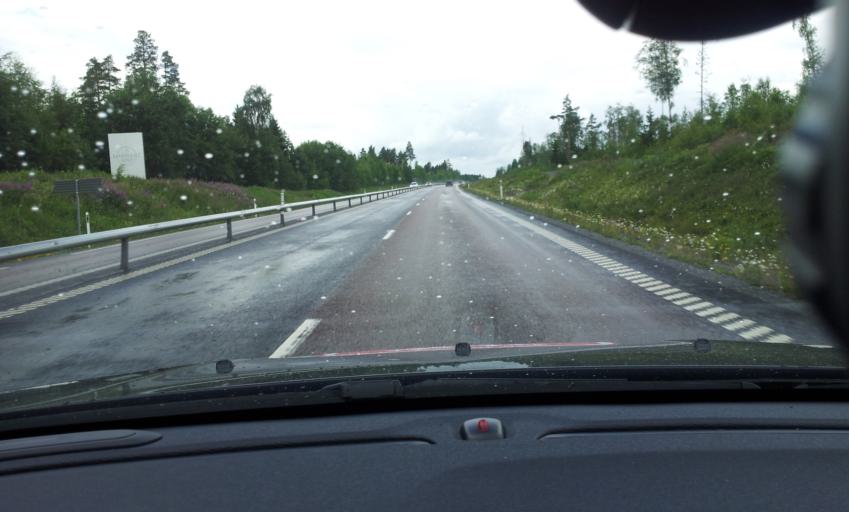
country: SE
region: Jaemtland
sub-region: Krokoms Kommun
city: Krokom
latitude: 63.2925
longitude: 14.5038
